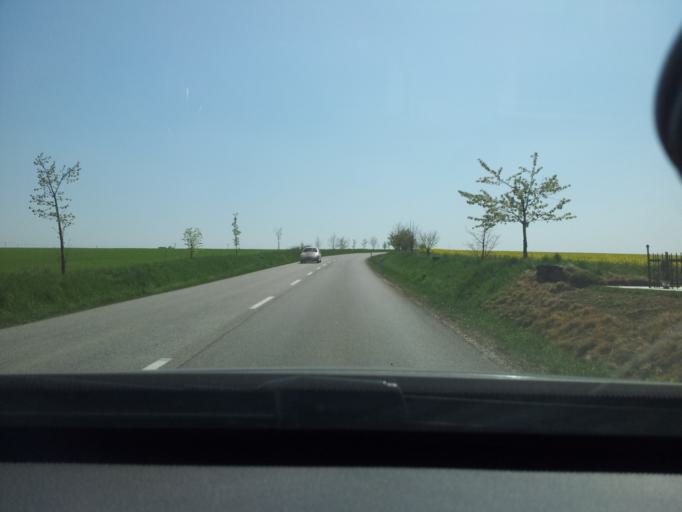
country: SK
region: Nitriansky
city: Zlate Moravce
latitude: 48.3786
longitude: 18.4005
